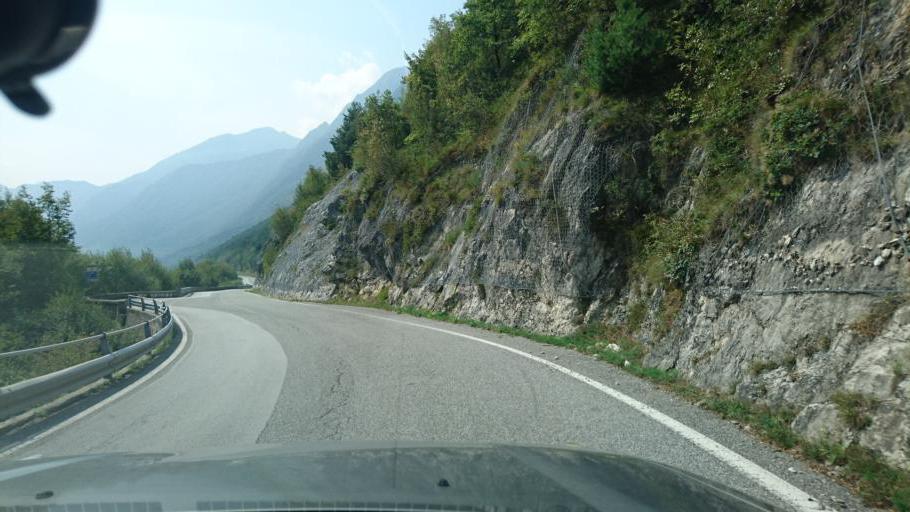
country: IT
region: Lombardy
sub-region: Provincia di Brescia
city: Ponte Caffaro
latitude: 45.8184
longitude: 10.5175
